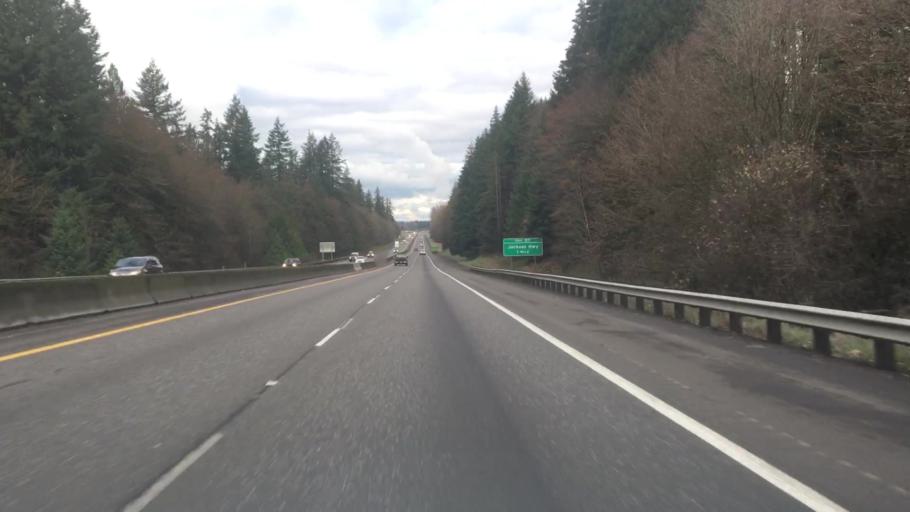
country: US
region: Washington
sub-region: Cowlitz County
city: Castle Rock
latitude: 46.3716
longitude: -122.9067
